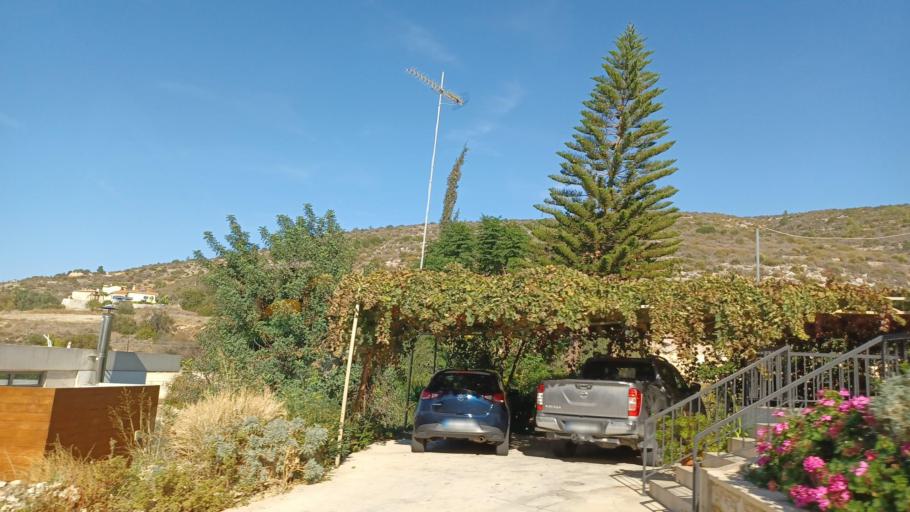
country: CY
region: Pafos
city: Polis
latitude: 34.9956
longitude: 32.4733
